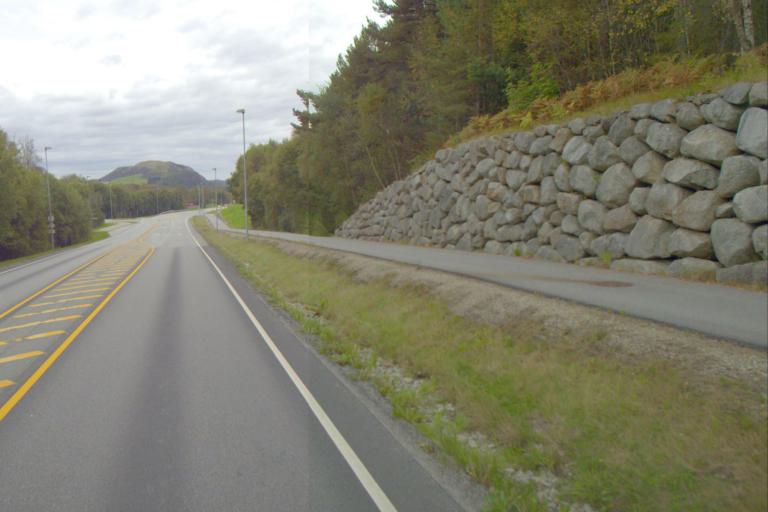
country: NO
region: Rogaland
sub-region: Sandnes
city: Hommersak
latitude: 58.8845
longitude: 5.8386
